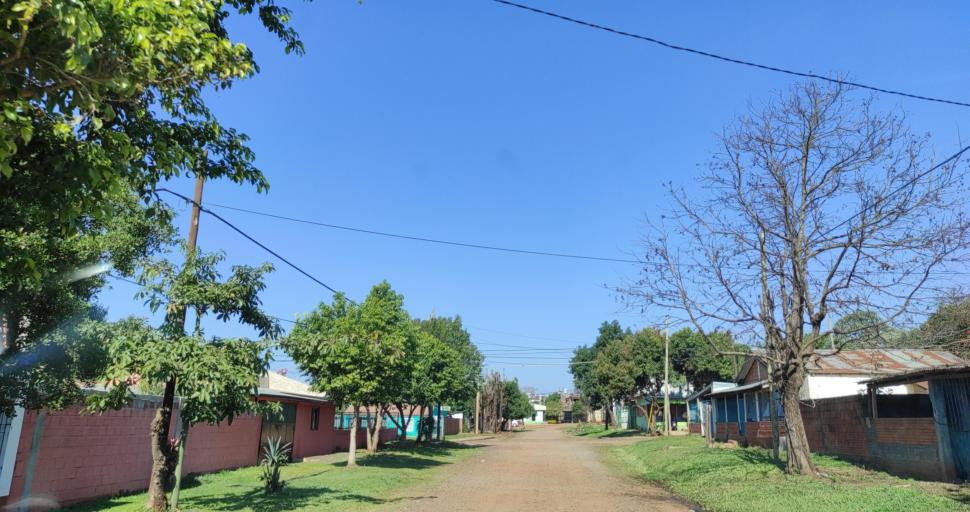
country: AR
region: Misiones
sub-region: Departamento de Capital
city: Posadas
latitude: -27.4124
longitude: -55.9093
